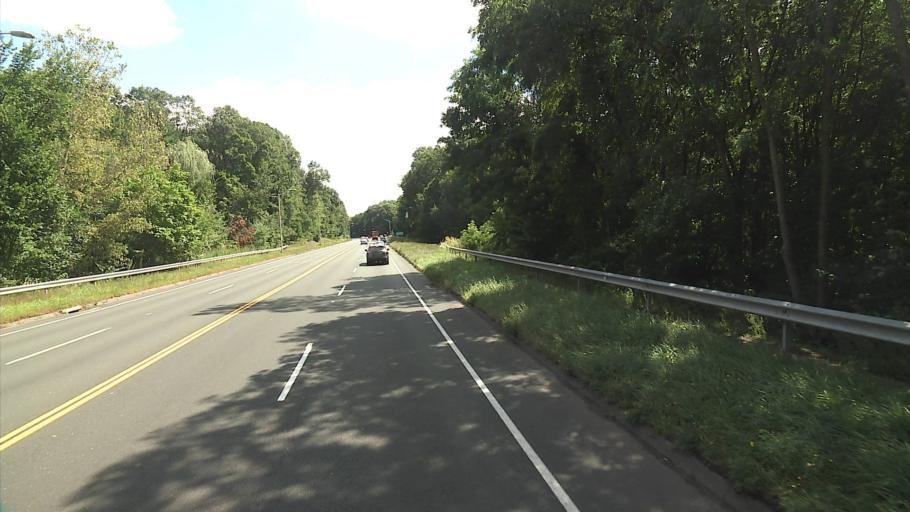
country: US
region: Connecticut
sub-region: Hartford County
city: Blue Hills
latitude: 41.8173
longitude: -72.6788
